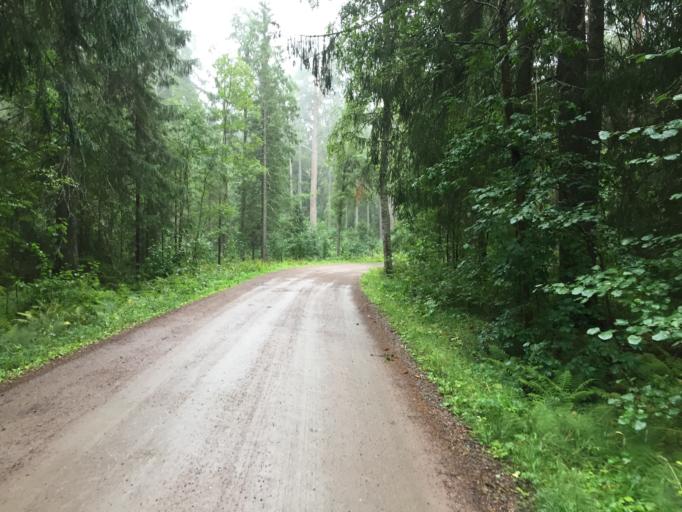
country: NO
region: Akershus
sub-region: Baerum
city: Lysaker
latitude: 59.9745
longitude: 10.6327
